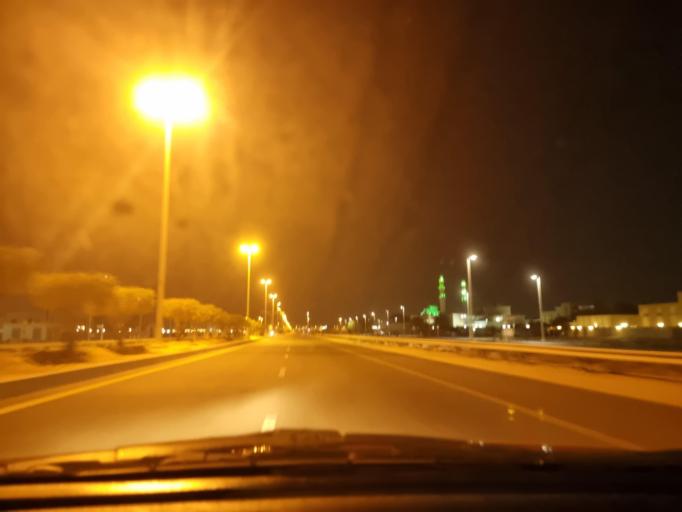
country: AE
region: Abu Dhabi
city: Abu Dhabi
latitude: 24.3720
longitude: 54.7011
